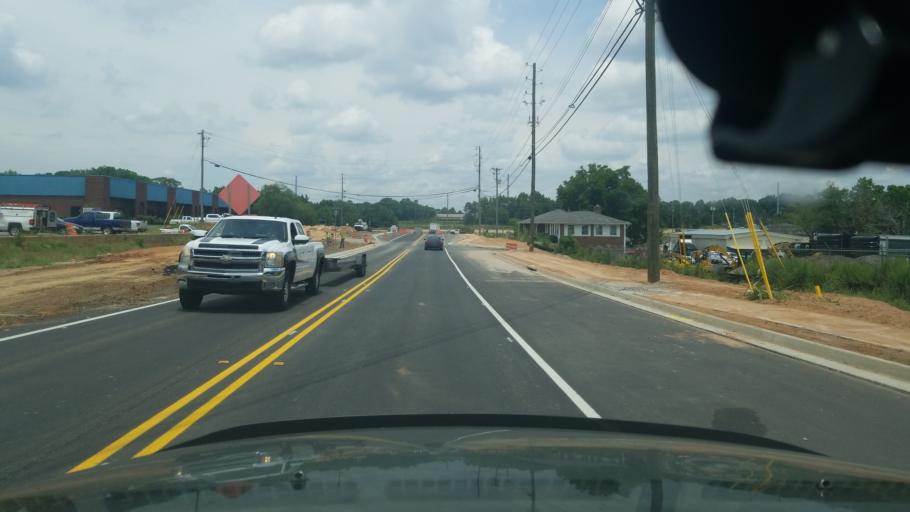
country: US
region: Georgia
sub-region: Fulton County
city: Milton
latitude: 34.1255
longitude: -84.2336
